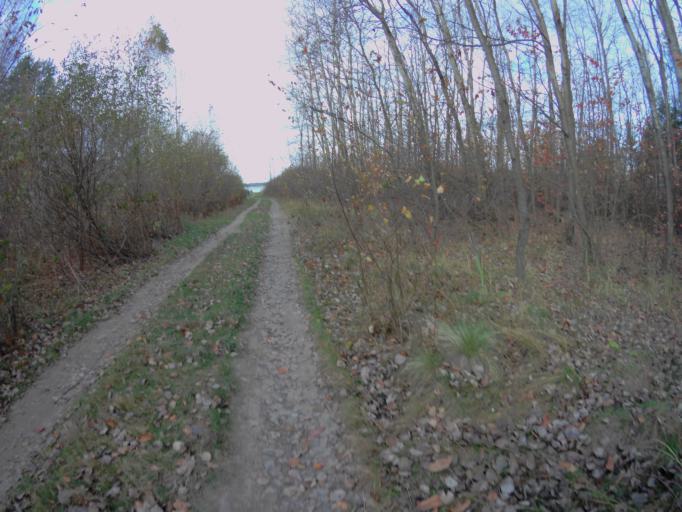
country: PL
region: Subcarpathian Voivodeship
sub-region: Powiat kolbuszowski
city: Lipnica
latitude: 50.3245
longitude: 21.9415
